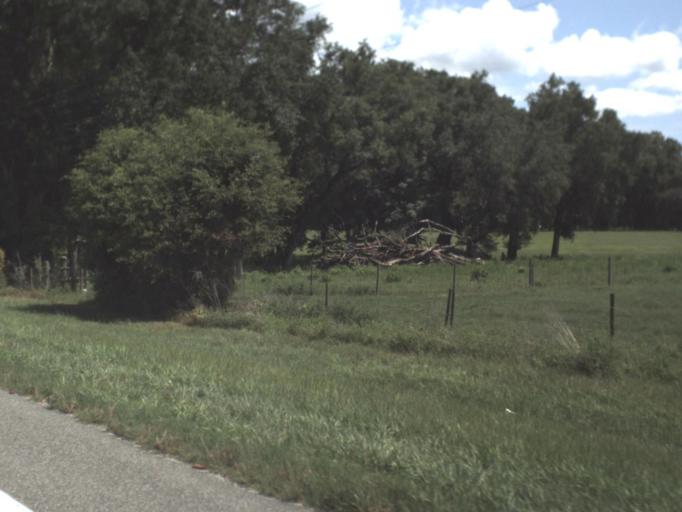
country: US
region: Florida
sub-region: Lafayette County
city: Mayo
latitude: 29.9777
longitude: -82.9907
